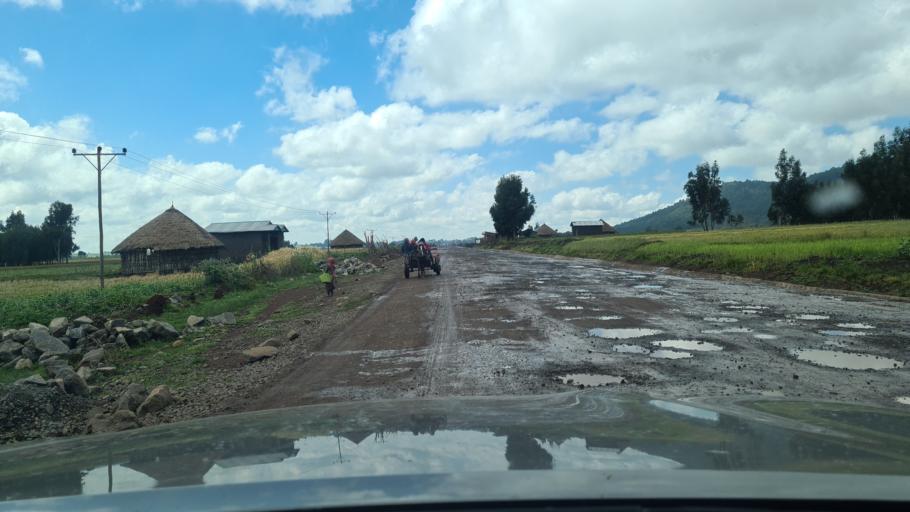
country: ET
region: Oromiya
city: Huruta
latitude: 8.0872
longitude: 39.5402
